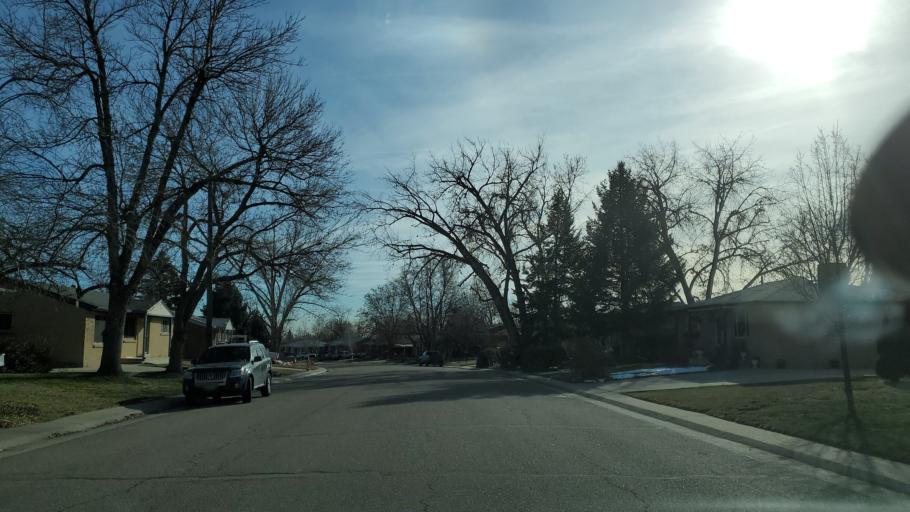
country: US
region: Colorado
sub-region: Adams County
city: Northglenn
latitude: 39.9126
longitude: -104.9629
